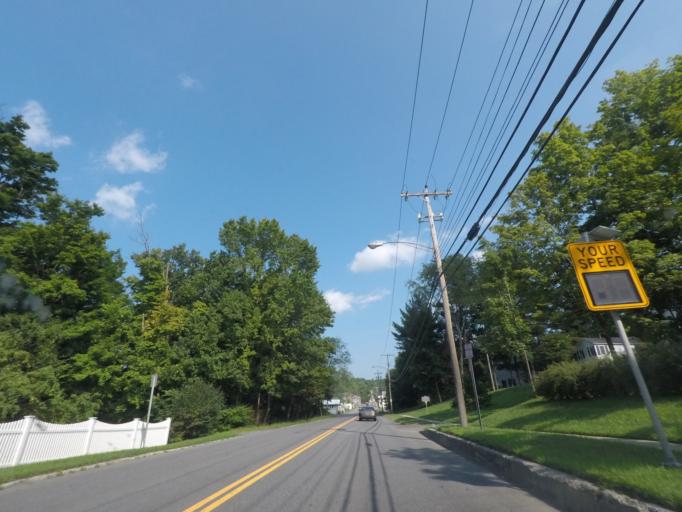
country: US
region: New York
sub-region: Rensselaer County
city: Nassau
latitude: 42.5169
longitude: -73.6144
